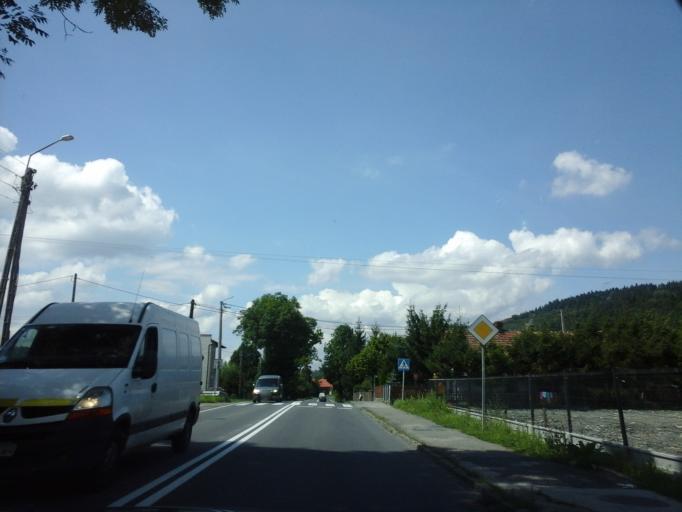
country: PL
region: Lesser Poland Voivodeship
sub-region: Powiat suski
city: Makow Podhalanski
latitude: 49.7310
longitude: 19.6662
